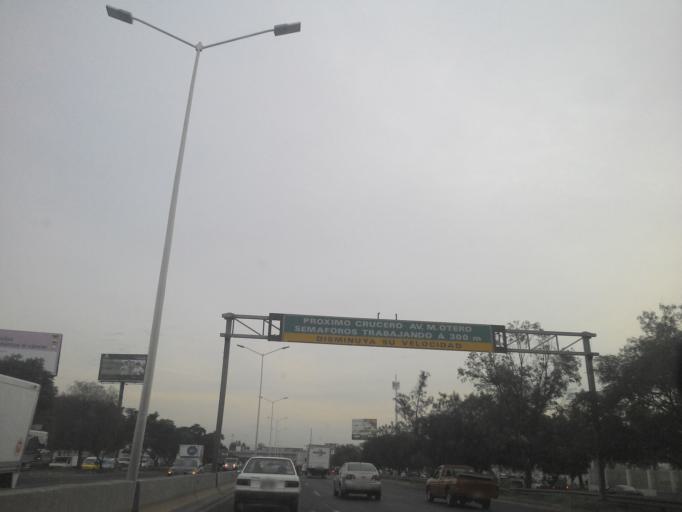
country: MX
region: Jalisco
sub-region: Tlajomulco de Zuniga
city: Palomar
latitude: 20.6338
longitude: -103.4374
